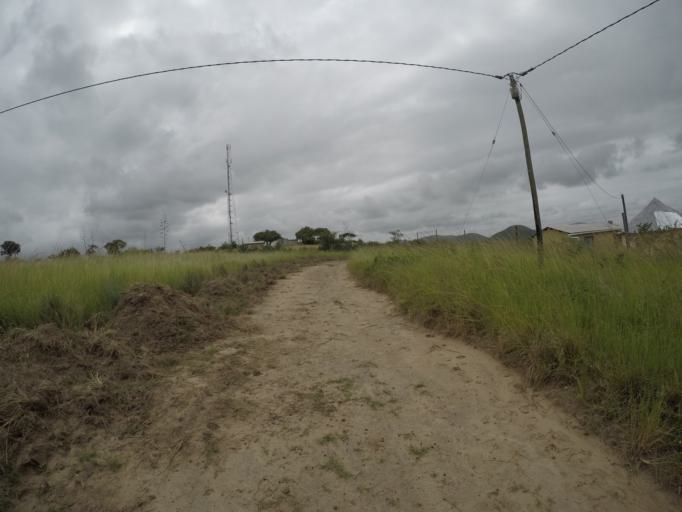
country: ZA
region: KwaZulu-Natal
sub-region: uThungulu District Municipality
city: Empangeni
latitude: -28.6056
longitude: 31.8348
